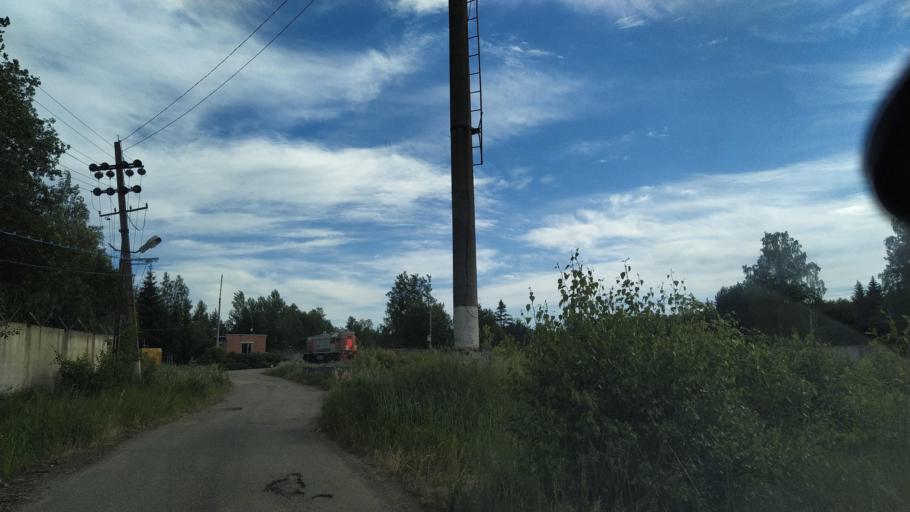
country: RU
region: Leningrad
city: Koltushi
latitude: 59.8669
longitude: 30.6692
